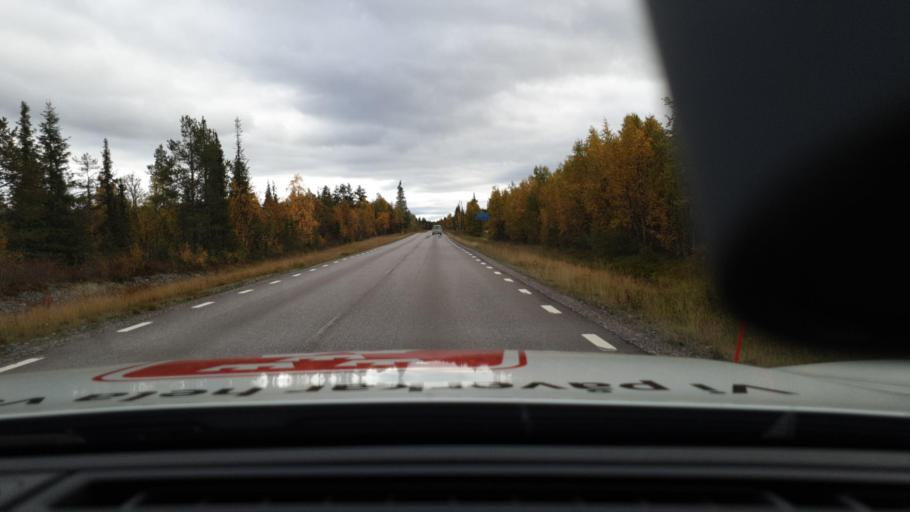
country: SE
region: Norrbotten
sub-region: Gallivare Kommun
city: Malmberget
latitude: 67.4279
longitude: 21.1319
